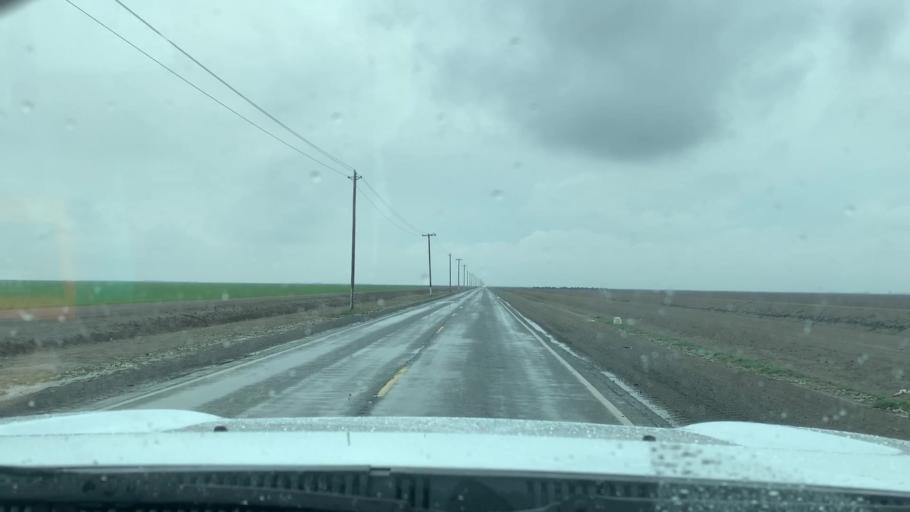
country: US
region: California
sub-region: Kings County
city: Corcoran
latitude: 35.9841
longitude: -119.5720
